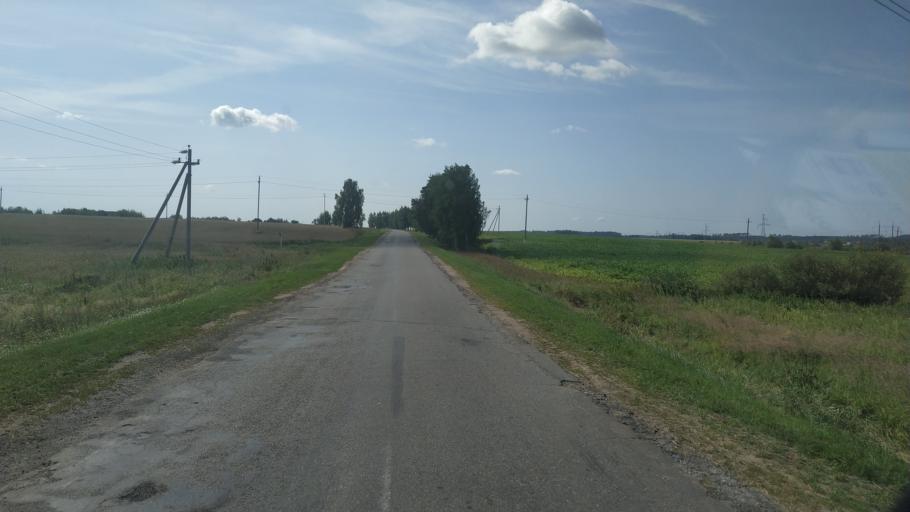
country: BY
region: Mogilev
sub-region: Mahilyowski Rayon
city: Veyno
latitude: 53.7889
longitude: 30.4324
